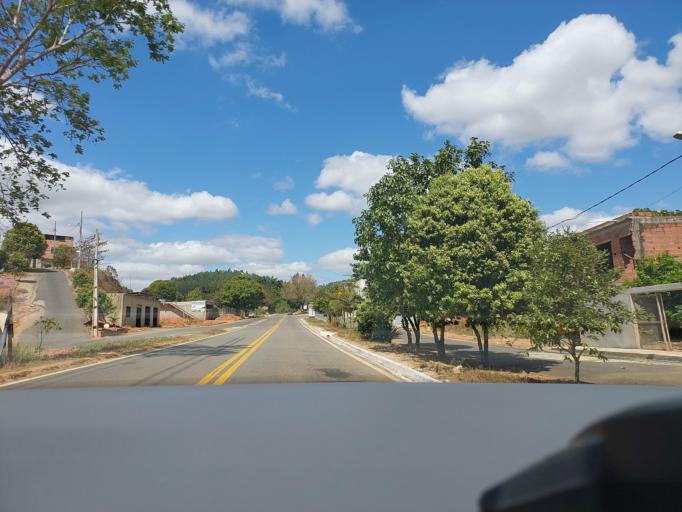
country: BR
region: Minas Gerais
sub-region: Muriae
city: Muriae
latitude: -21.1068
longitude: -42.4568
